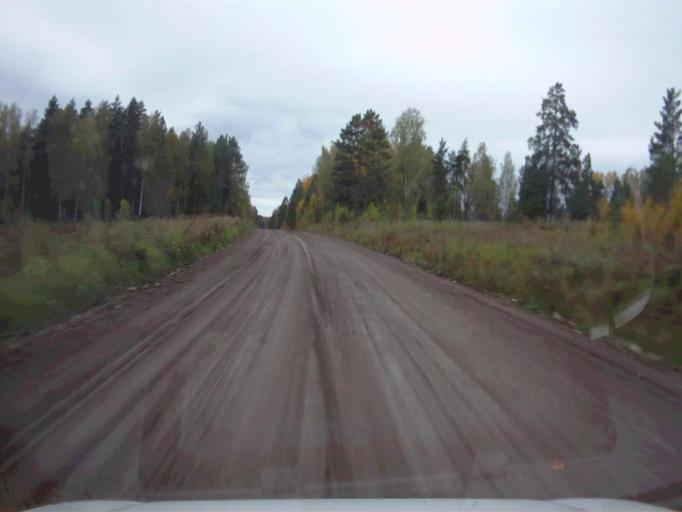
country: RU
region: Chelyabinsk
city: Nyazepetrovsk
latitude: 56.0913
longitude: 59.4124
